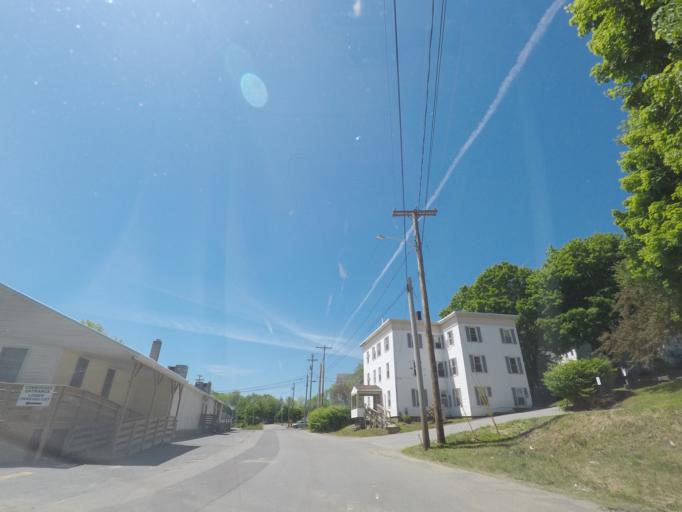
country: US
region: Maine
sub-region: Kennebec County
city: Gardiner
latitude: 44.2307
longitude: -69.7773
